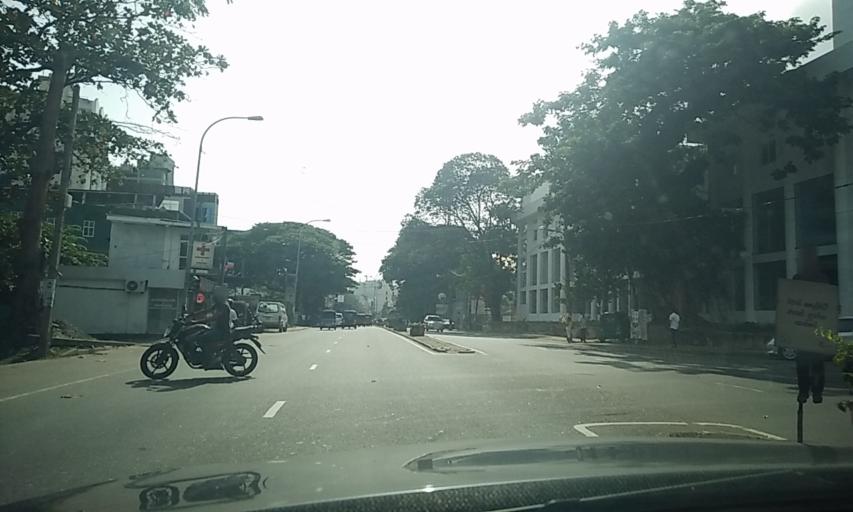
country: LK
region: Western
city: Pita Kotte
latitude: 6.8777
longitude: 79.8783
